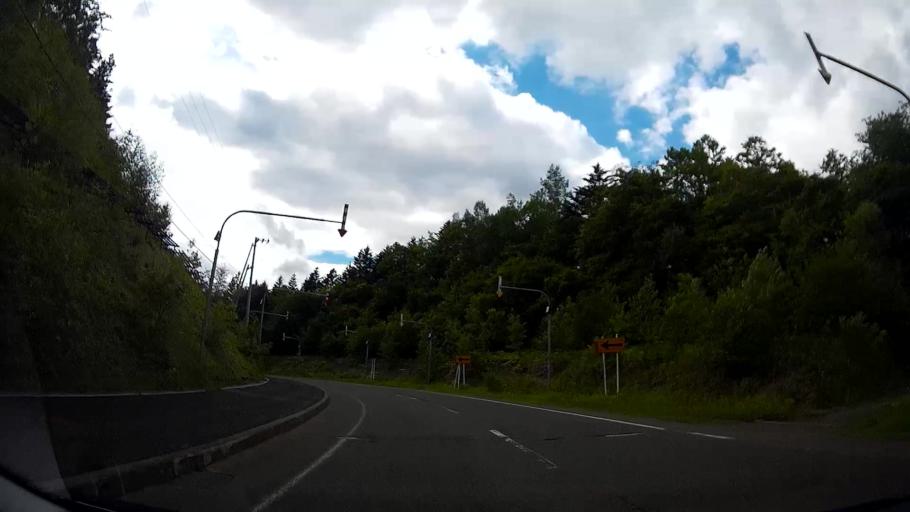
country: JP
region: Hokkaido
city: Kitahiroshima
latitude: 42.8437
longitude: 141.4462
